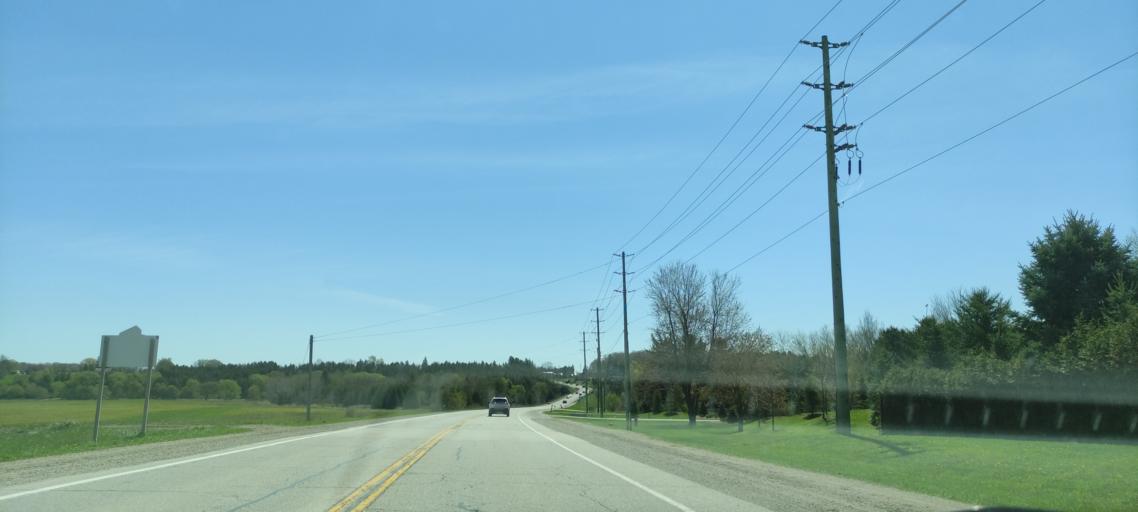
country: CA
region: Ontario
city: Waterloo
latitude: 43.5914
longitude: -80.4770
